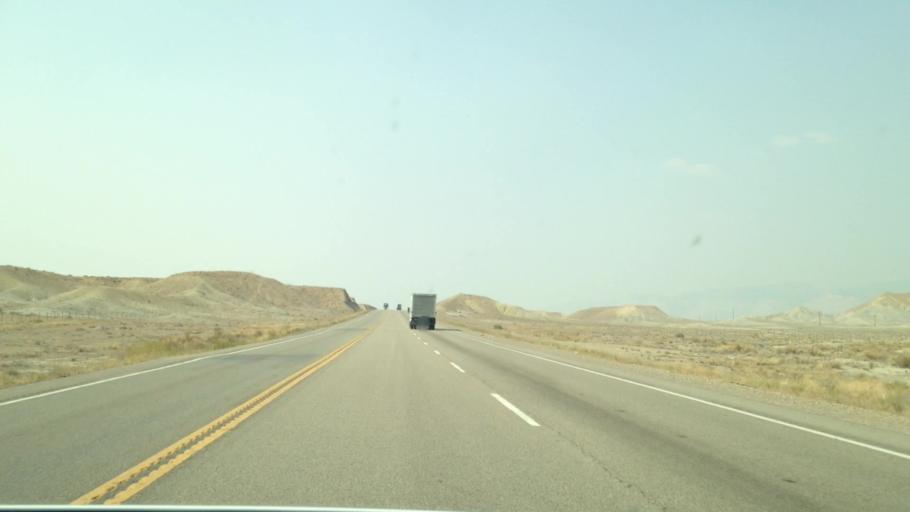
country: US
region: Utah
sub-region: Carbon County
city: East Carbon City
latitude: 39.2723
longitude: -110.3472
